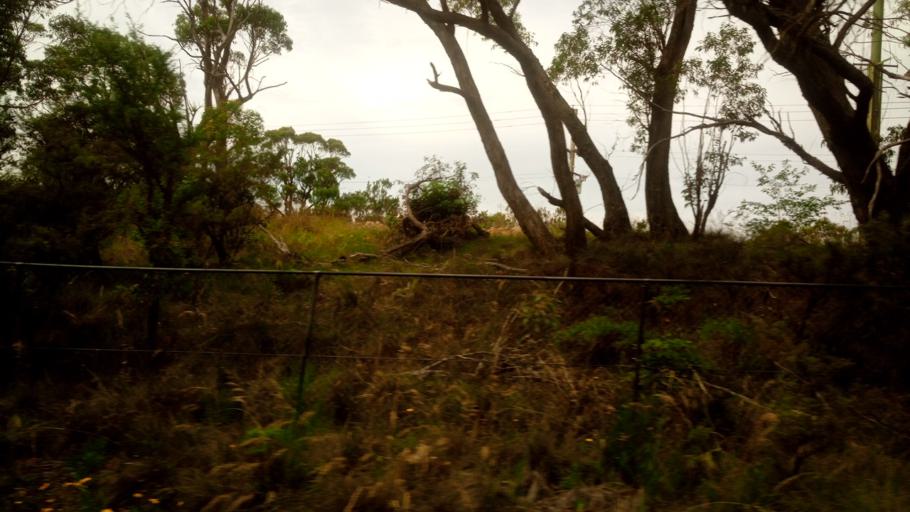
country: AU
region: New South Wales
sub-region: Blue Mountains Municipality
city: Leura
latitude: -33.7086
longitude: 150.3534
